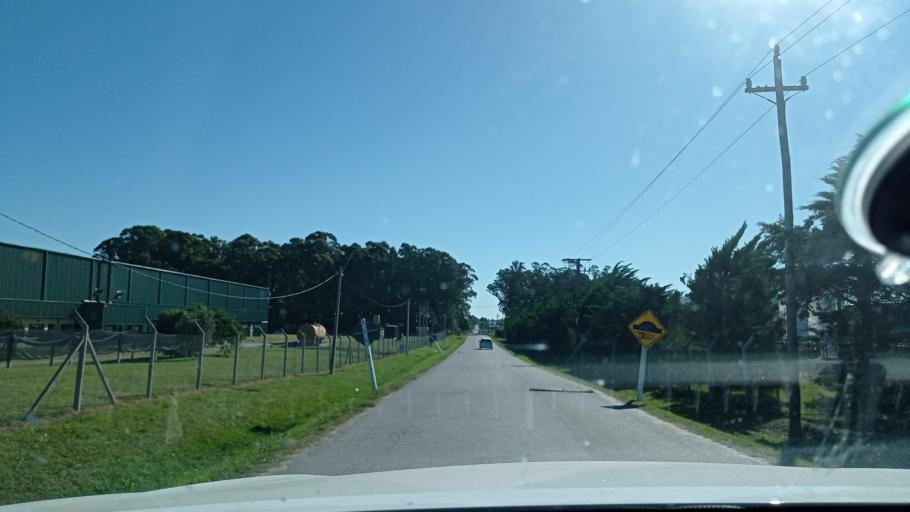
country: UY
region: Canelones
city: Pando
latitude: -34.7581
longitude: -55.9820
